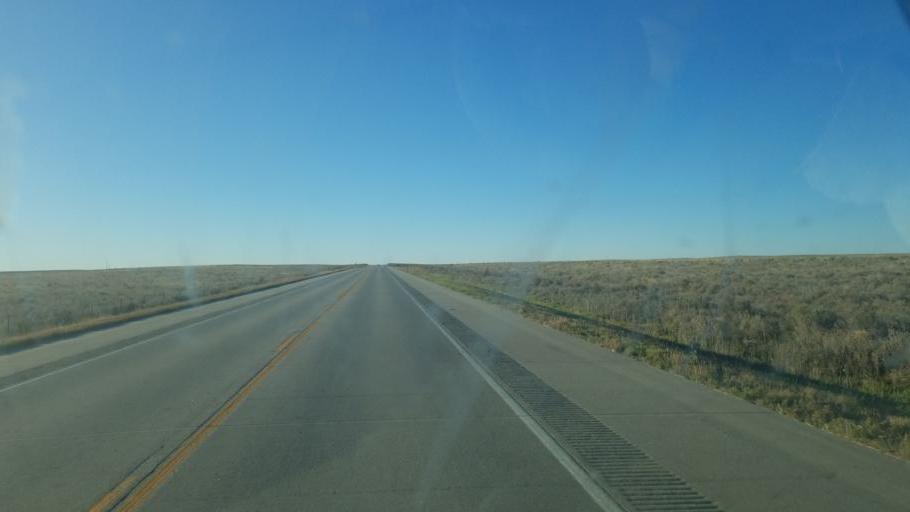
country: US
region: Colorado
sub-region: Kiowa County
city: Eads
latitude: 38.5486
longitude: -102.7860
